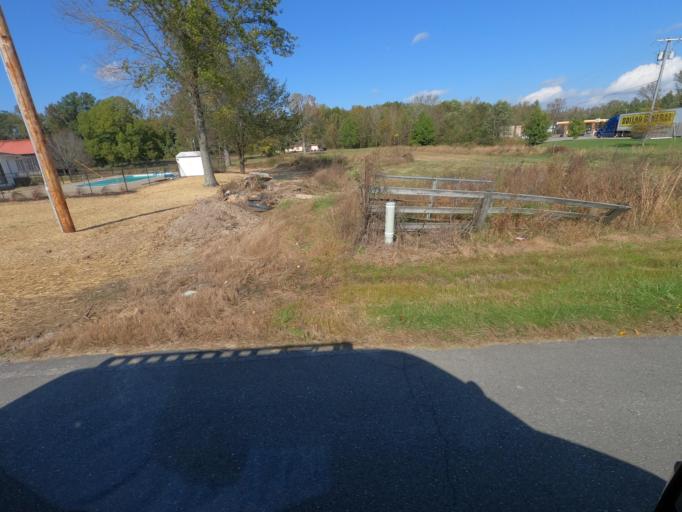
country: US
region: Tennessee
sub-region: Cheatham County
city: Pleasant View
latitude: 36.4423
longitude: -87.1036
